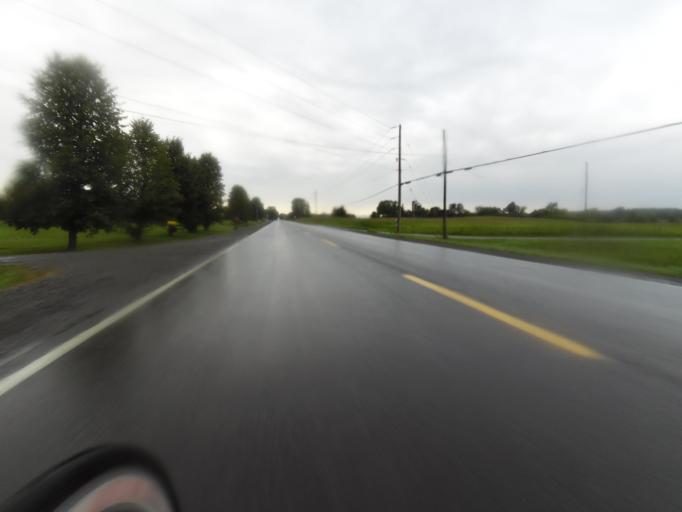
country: CA
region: Ontario
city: Bells Corners
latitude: 45.1992
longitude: -75.6922
